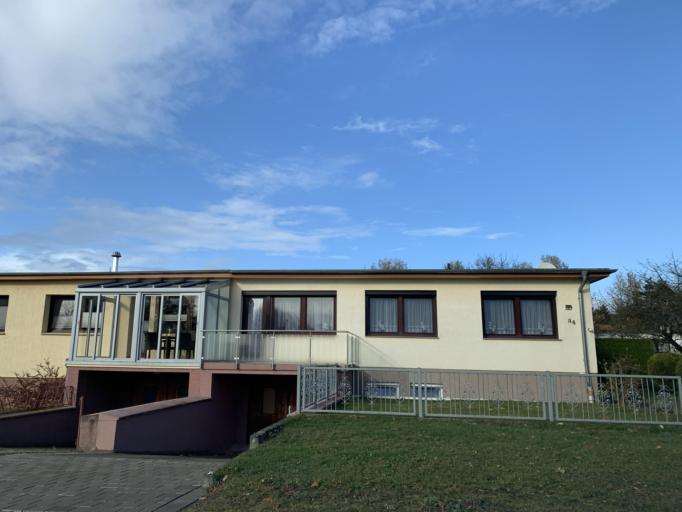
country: DE
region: Mecklenburg-Vorpommern
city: Blankensee
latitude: 53.4042
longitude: 13.2687
